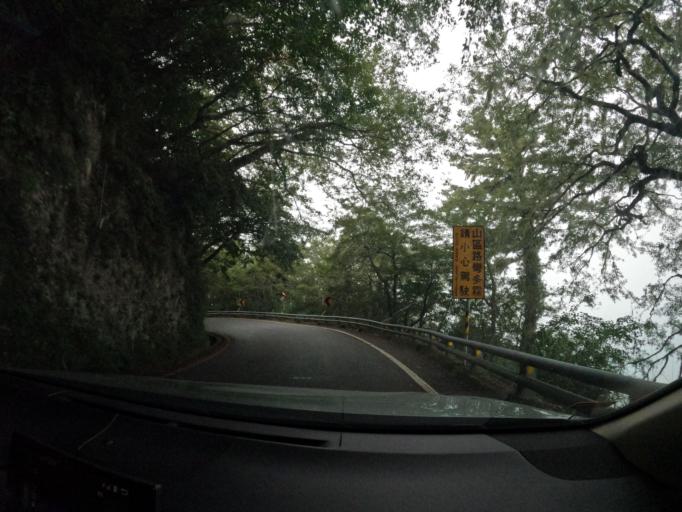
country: TW
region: Taiwan
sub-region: Taitung
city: Taitung
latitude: 23.2431
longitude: 120.9849
